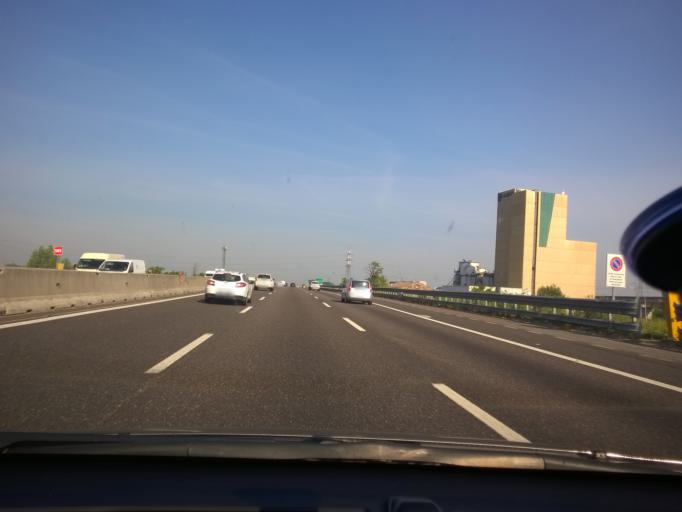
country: IT
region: Emilia-Romagna
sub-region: Provincia di Parma
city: San Prospero
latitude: 44.8240
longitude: 10.3864
